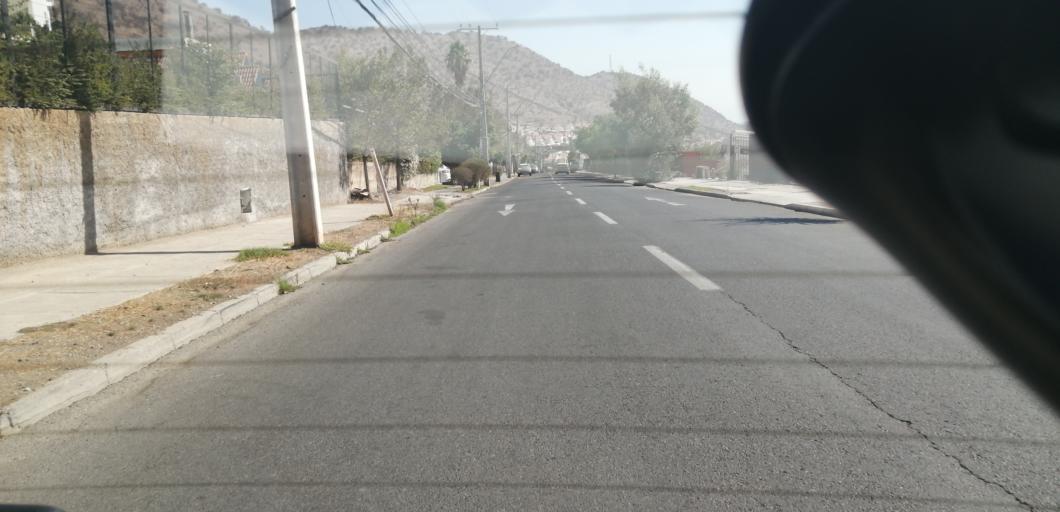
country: CL
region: Santiago Metropolitan
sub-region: Provincia de Santiago
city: Lo Prado
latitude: -33.4540
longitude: -70.8222
